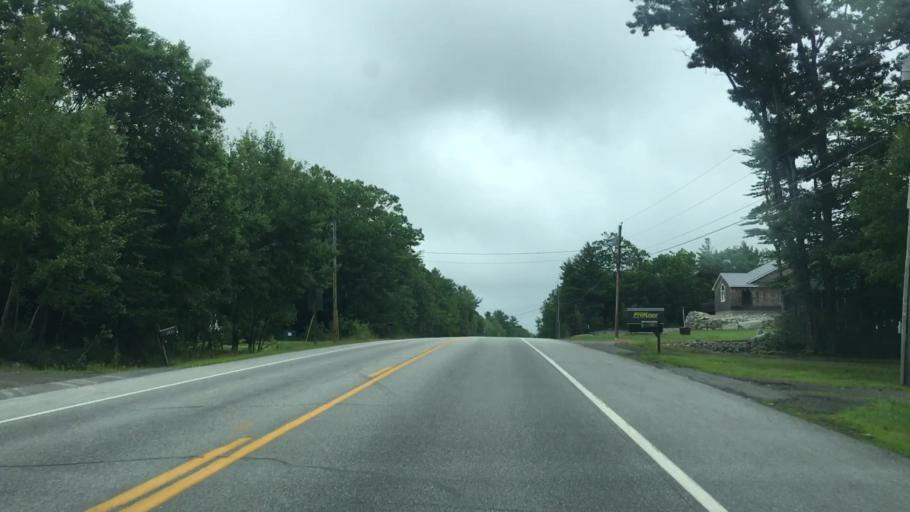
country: US
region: Maine
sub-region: Kennebec County
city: Windsor
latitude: 44.2752
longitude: -69.6458
